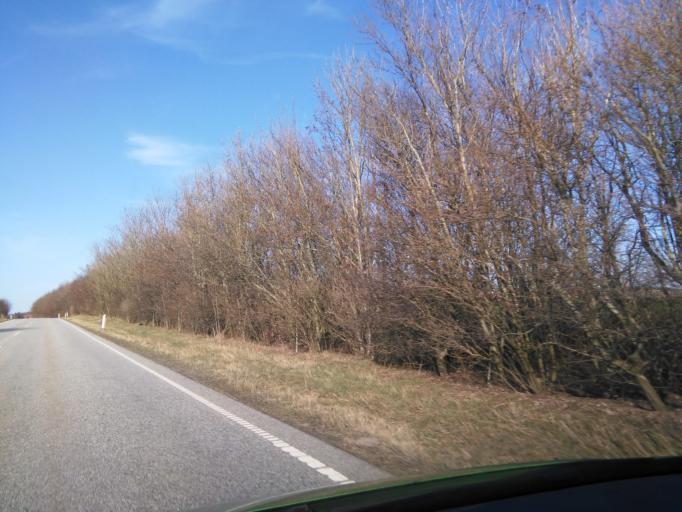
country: DK
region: Central Jutland
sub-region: Horsens Kommune
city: Braedstrup
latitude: 55.9141
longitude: 9.6690
